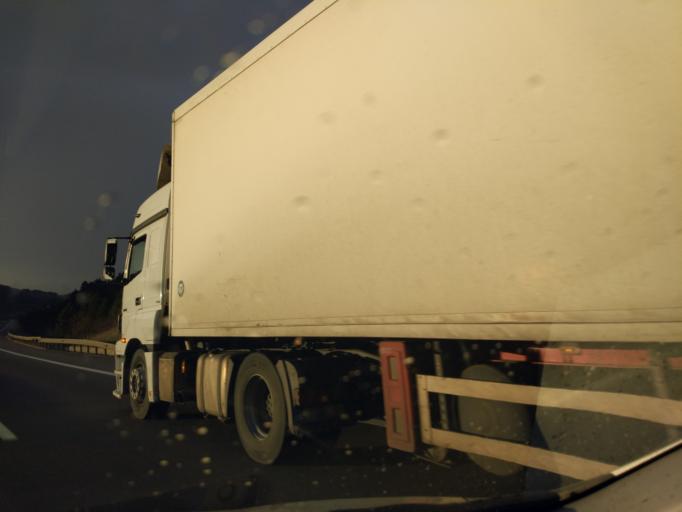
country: TR
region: Bolu
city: Bolu
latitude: 40.7347
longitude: 31.8039
